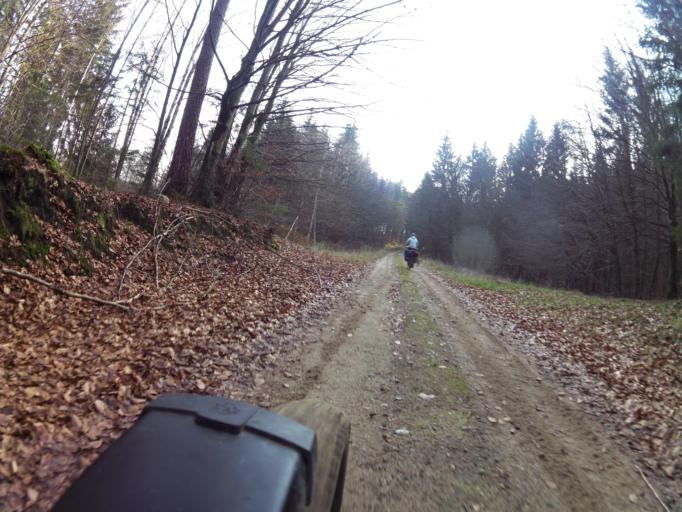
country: PL
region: West Pomeranian Voivodeship
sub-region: Powiat koszalinski
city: Polanow
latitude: 54.1726
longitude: 16.7267
